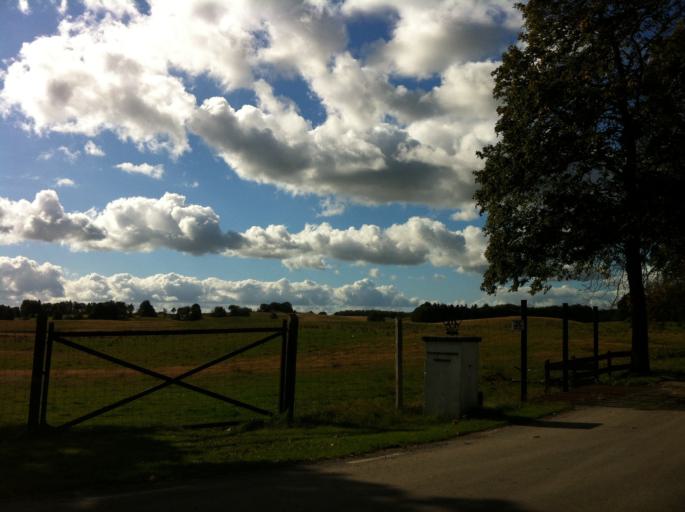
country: SE
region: Skane
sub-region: Kristianstads Kommun
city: Degeberga
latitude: 55.7139
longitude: 13.9699
